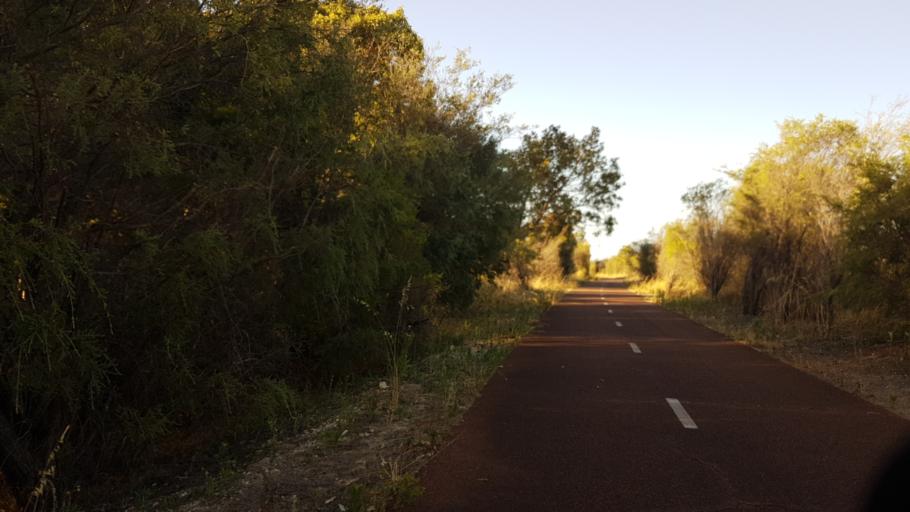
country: AU
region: Western Australia
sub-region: Kwinana
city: Bertram
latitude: -32.2483
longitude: 115.8522
